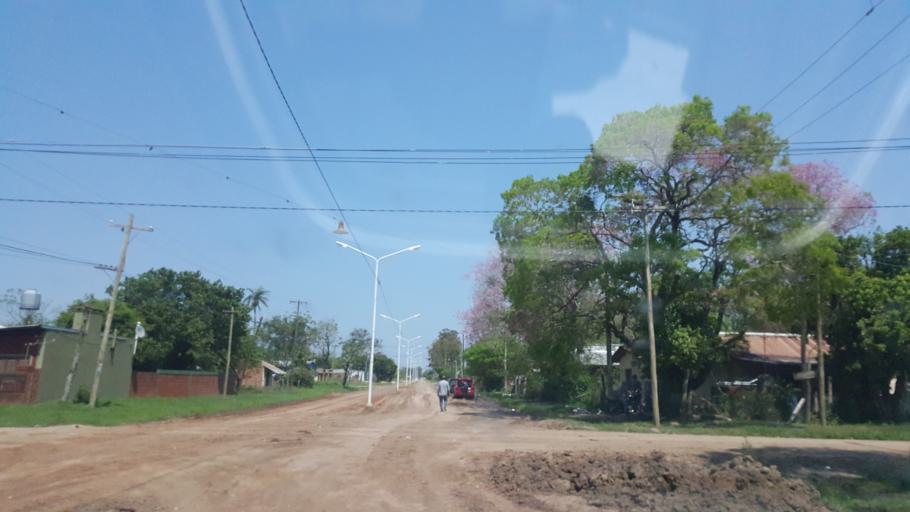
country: AR
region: Corrientes
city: Ita Ibate
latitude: -27.4256
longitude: -57.3419
